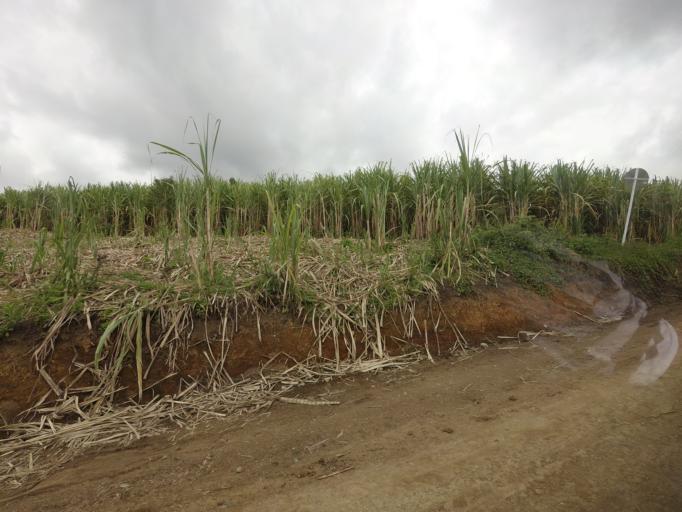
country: CO
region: Huila
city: San Agustin
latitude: 1.9438
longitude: -76.2969
